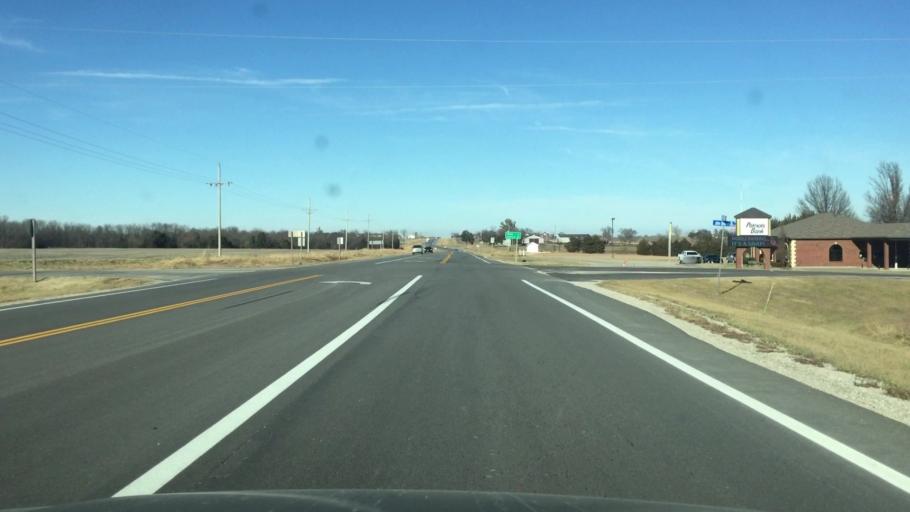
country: US
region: Kansas
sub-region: Franklin County
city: Ottawa
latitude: 38.4916
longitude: -95.2672
